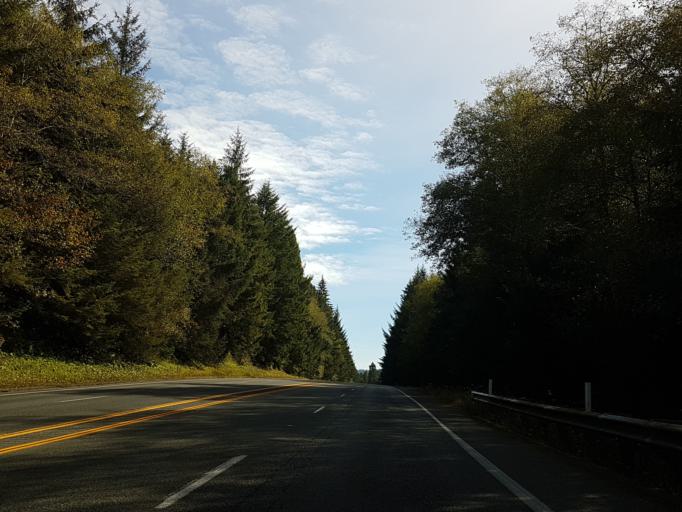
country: US
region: California
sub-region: Del Norte County
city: Bertsch-Oceanview
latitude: 41.4832
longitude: -124.0506
